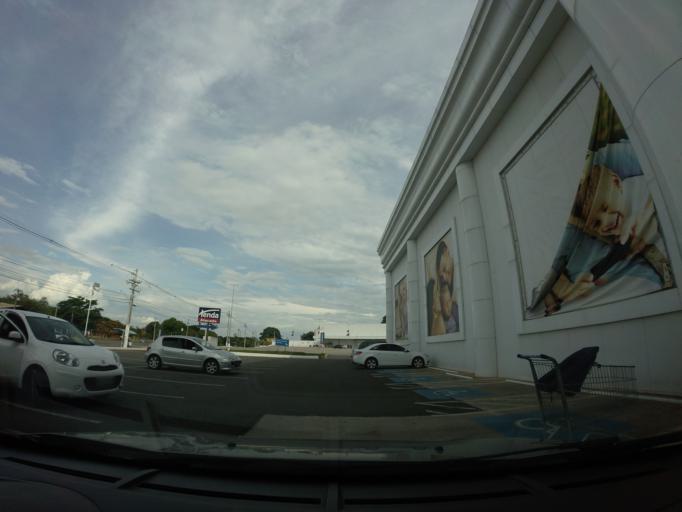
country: BR
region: Sao Paulo
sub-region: Piracicaba
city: Piracicaba
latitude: -22.7350
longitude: -47.6069
